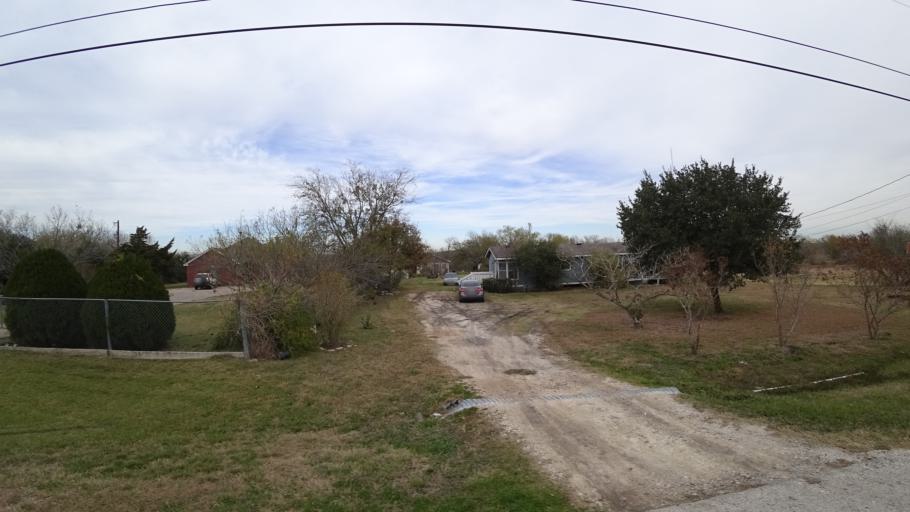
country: US
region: Texas
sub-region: Travis County
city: Garfield
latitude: 30.1171
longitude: -97.5819
